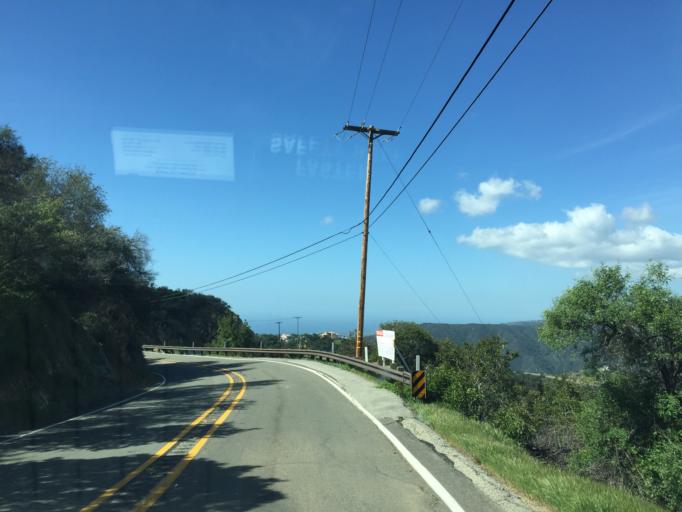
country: US
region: California
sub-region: Los Angeles County
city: Malibu Beach
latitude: 34.0695
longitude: -118.6700
